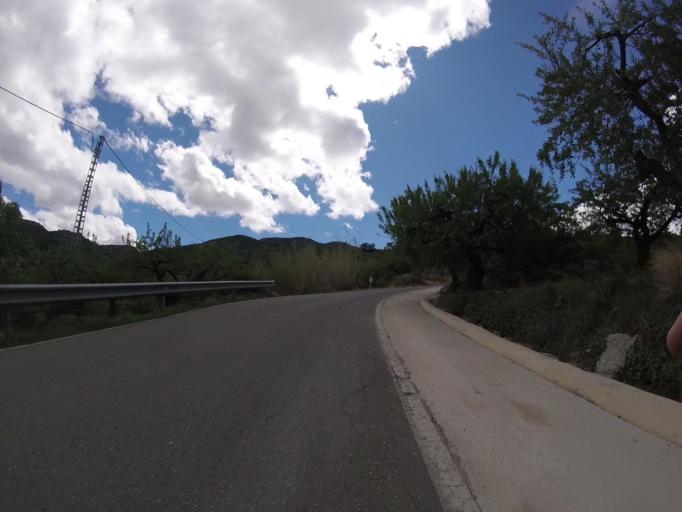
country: ES
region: Valencia
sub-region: Provincia de Castello
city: Sierra-Engarceran
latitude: 40.2956
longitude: -0.0409
